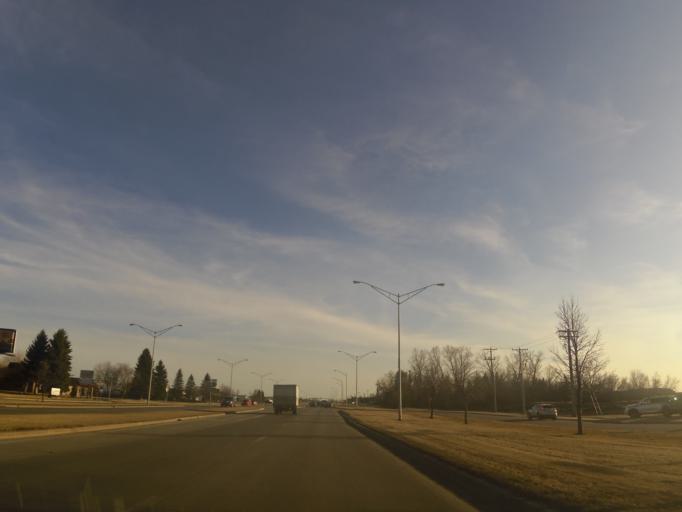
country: US
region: North Dakota
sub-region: Grand Forks County
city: Grand Forks
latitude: 47.8884
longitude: -97.0454
